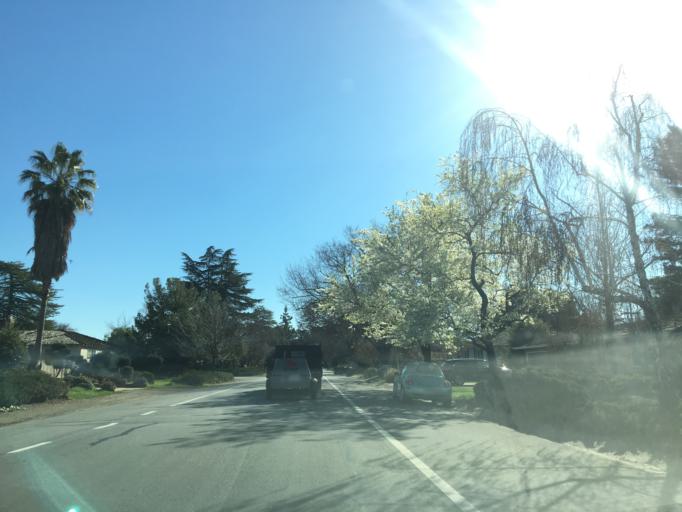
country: US
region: California
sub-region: Santa Clara County
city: Loyola
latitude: 37.3544
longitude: -122.0688
